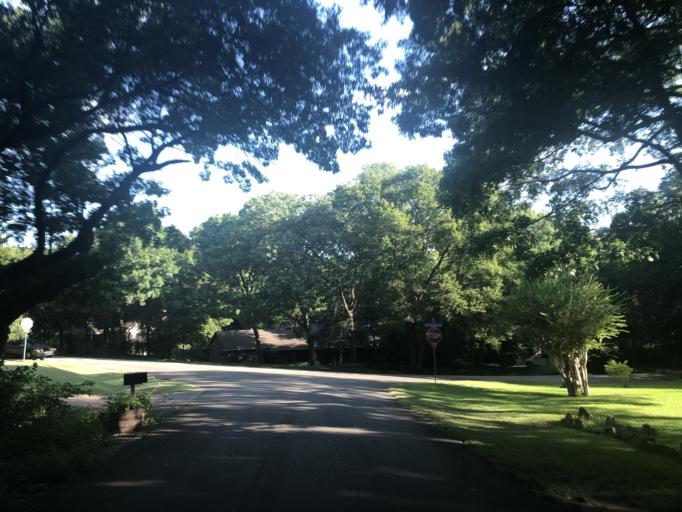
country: US
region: Texas
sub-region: Dallas County
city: Duncanville
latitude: 32.6732
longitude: -96.9179
